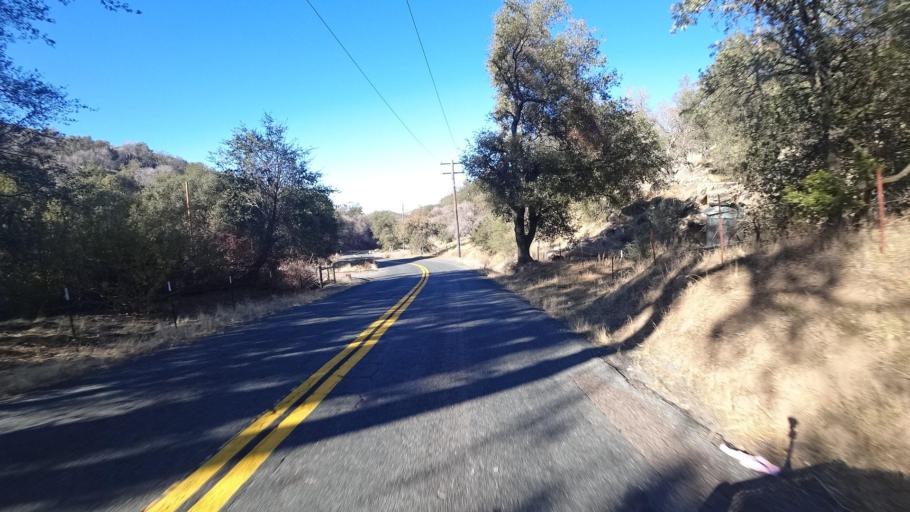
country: US
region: California
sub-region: Kern County
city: Alta Sierra
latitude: 35.7907
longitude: -118.7385
